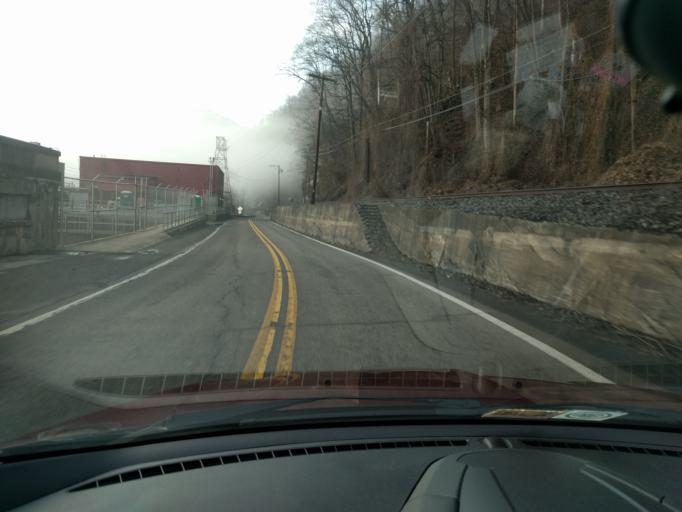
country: US
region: West Virginia
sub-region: Fayette County
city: Ansted
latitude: 38.1487
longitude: -81.2150
